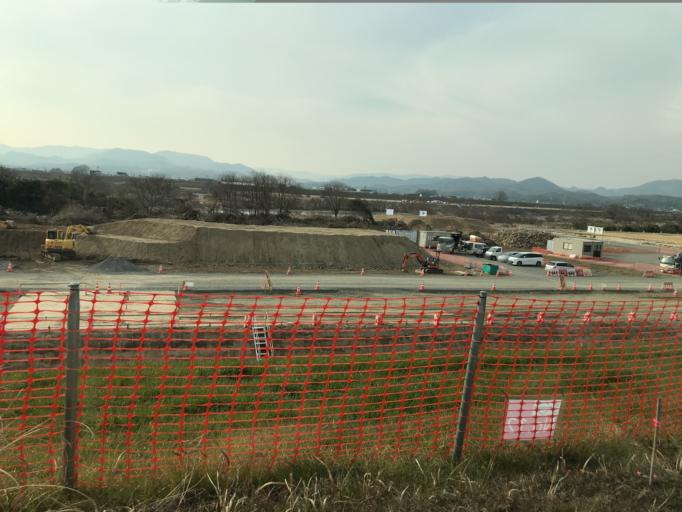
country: JP
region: Okayama
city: Soja
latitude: 34.6360
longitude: 133.7308
